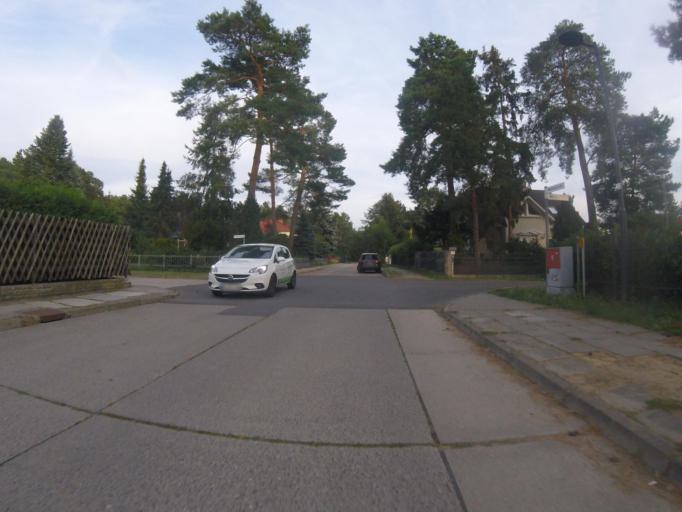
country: DE
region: Brandenburg
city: Zeuthen
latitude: 52.3439
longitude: 13.6158
